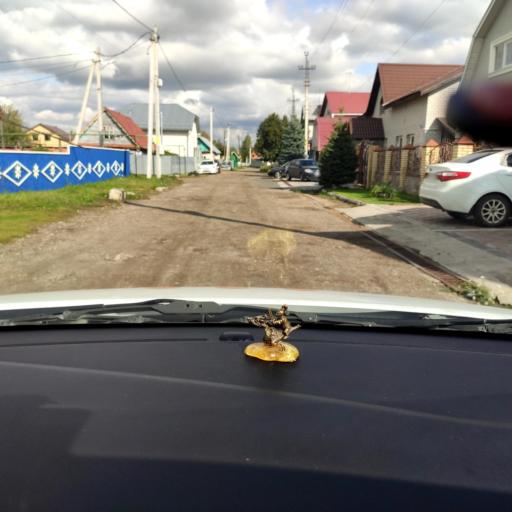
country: RU
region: Tatarstan
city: Stolbishchi
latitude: 55.6902
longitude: 49.1438
